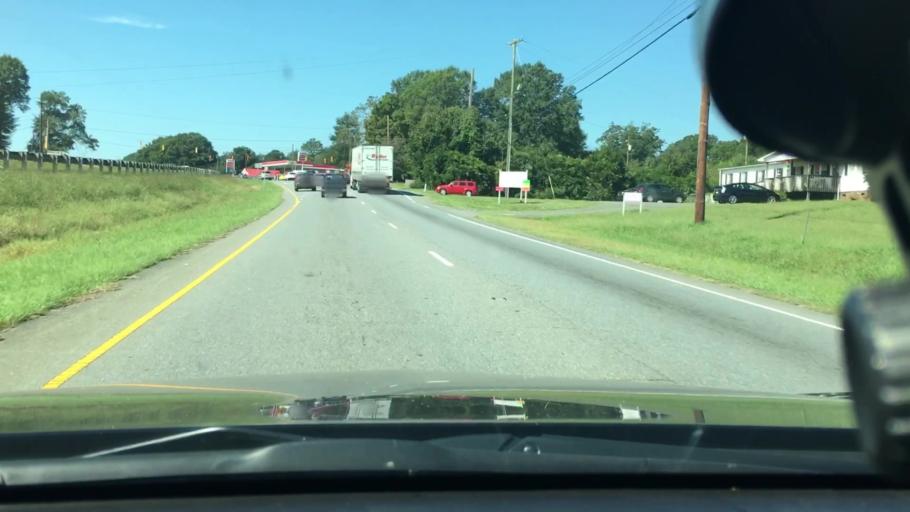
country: US
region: North Carolina
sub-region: Cleveland County
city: Boiling Springs
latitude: 35.2944
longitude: -81.6131
